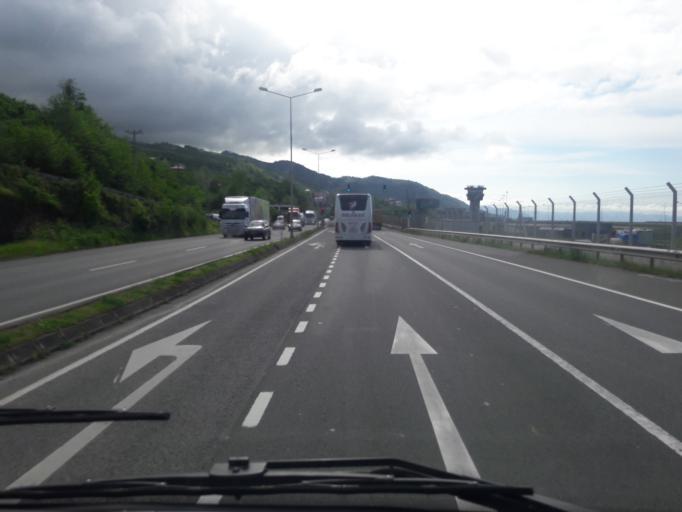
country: TR
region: Ordu
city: Gulyali
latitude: 40.9629
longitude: 38.0879
